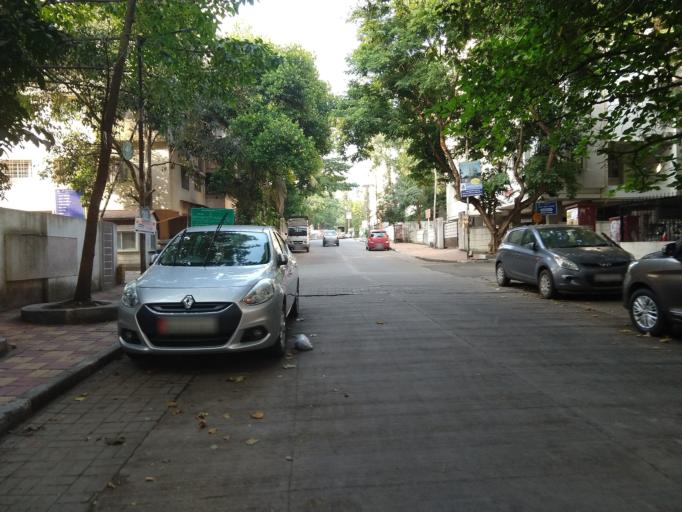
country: IN
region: Maharashtra
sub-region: Pune Division
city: Shivaji Nagar
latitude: 18.5096
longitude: 73.7932
